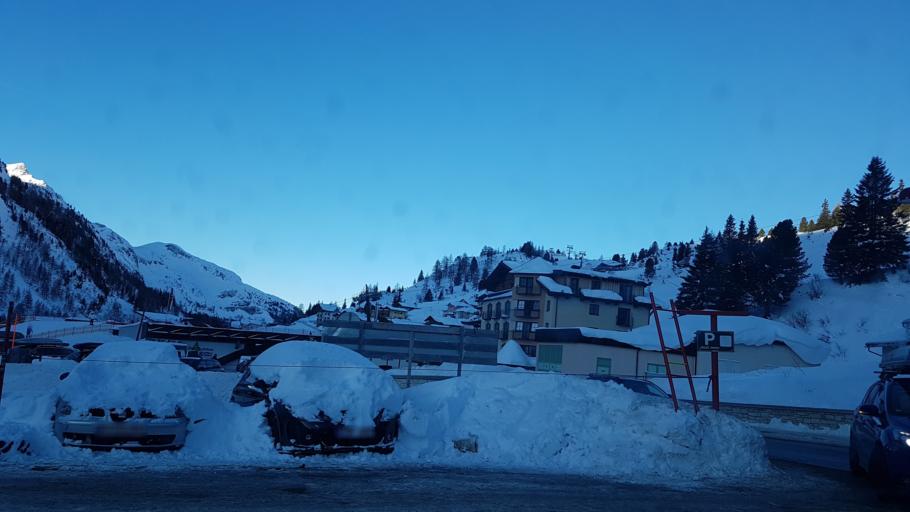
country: AT
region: Salzburg
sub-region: Politischer Bezirk Sankt Johann im Pongau
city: Untertauern
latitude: 47.2518
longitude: 13.5462
